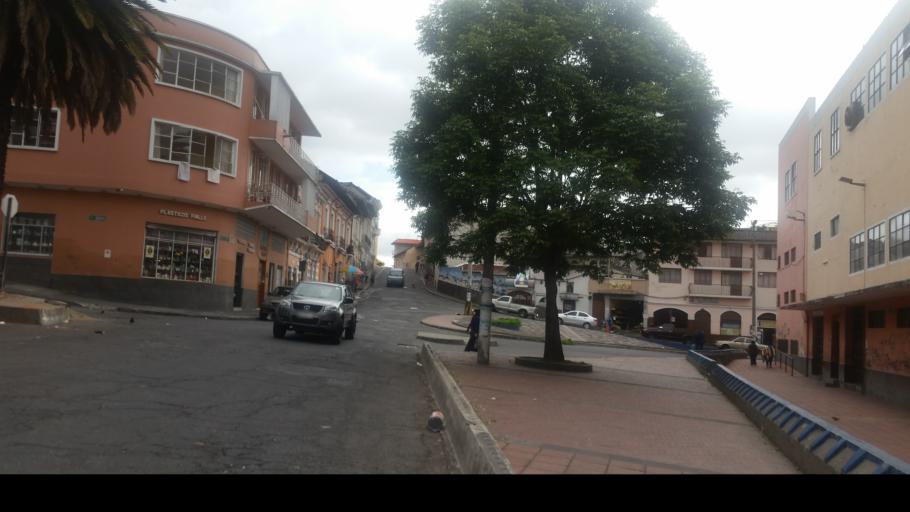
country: EC
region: Pichincha
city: Quito
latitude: -0.2206
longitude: -78.5071
